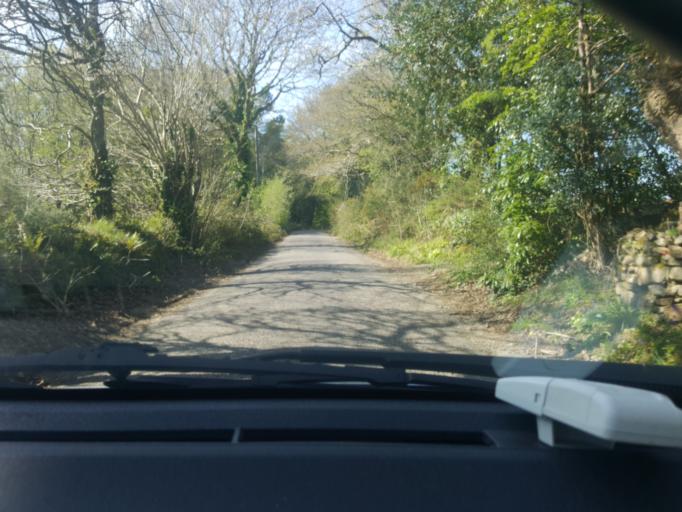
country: IE
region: Munster
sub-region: County Cork
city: Bandon
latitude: 51.7676
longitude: -8.6829
